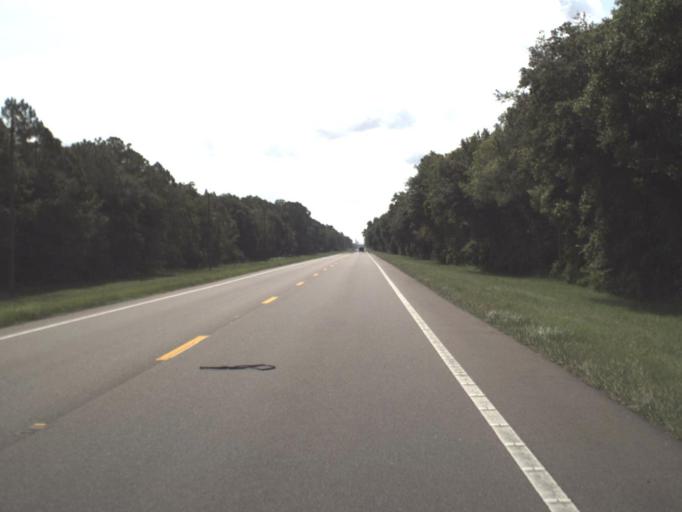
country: US
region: Florida
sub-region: Pasco County
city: Zephyrhills North
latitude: 28.2762
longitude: -82.1061
